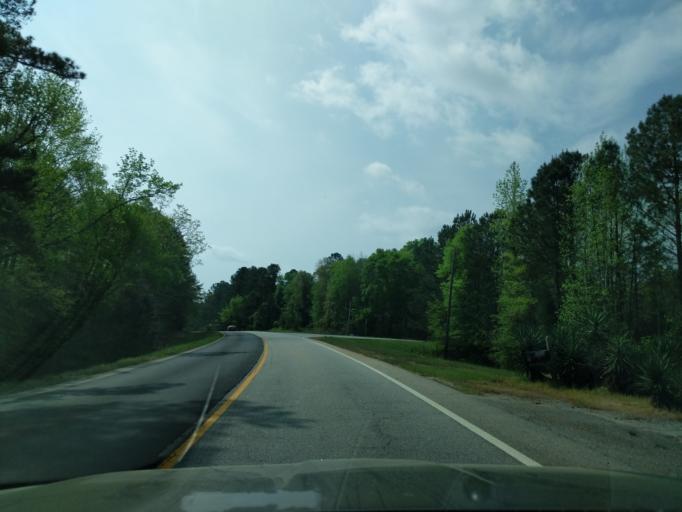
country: US
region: Georgia
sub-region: Lincoln County
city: Lincolnton
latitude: 33.7809
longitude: -82.3818
